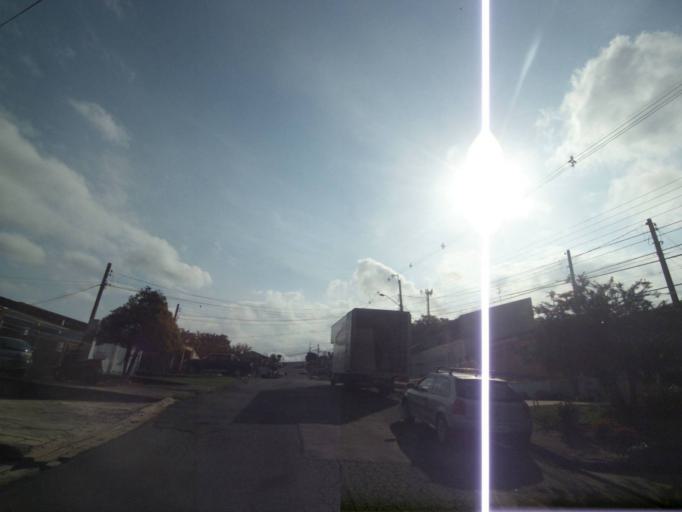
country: BR
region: Parana
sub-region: Pinhais
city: Pinhais
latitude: -25.4059
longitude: -49.1971
